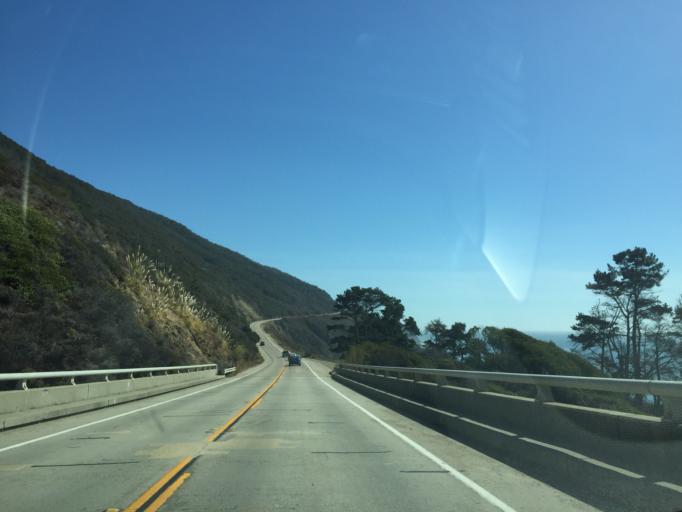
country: US
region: California
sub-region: Monterey County
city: Greenfield
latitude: 36.0444
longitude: -121.5846
